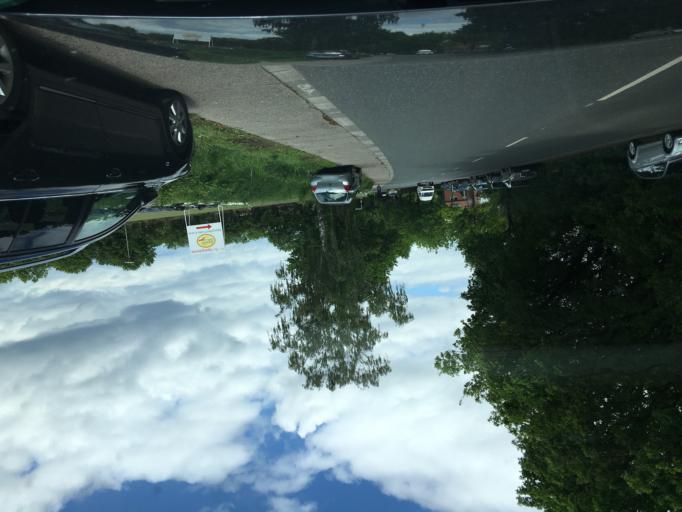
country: DE
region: North Rhine-Westphalia
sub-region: Regierungsbezirk Munster
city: Muenster
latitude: 52.0277
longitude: 7.6787
